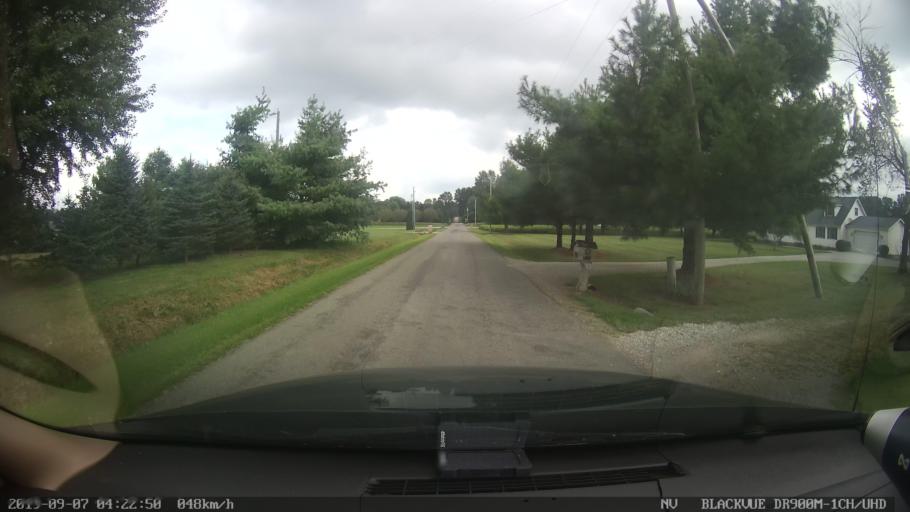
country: US
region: Ohio
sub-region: Knox County
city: Centerburg
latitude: 40.2746
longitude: -82.6713
